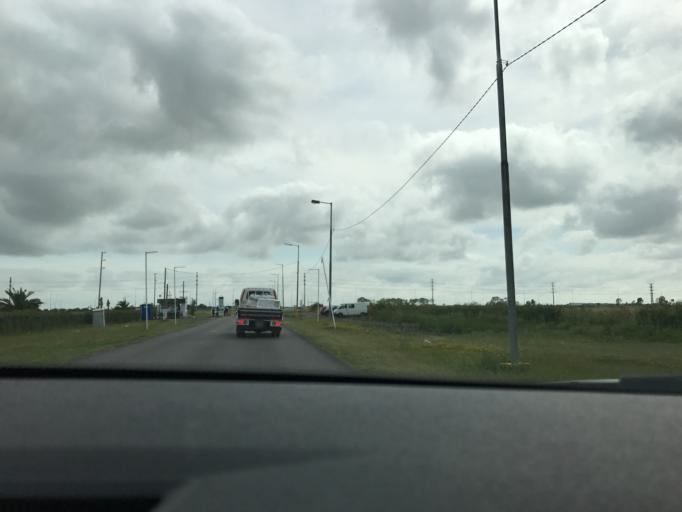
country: AR
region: Buenos Aires
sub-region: Partido de La Plata
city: La Plata
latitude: -34.8424
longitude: -58.0733
